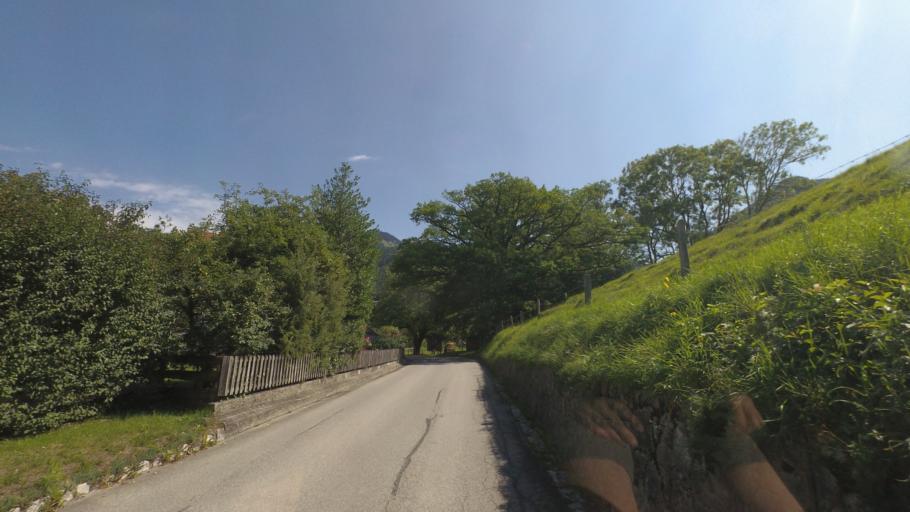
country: DE
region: Bavaria
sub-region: Upper Bavaria
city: Unterwossen
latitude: 47.7339
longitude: 12.4659
